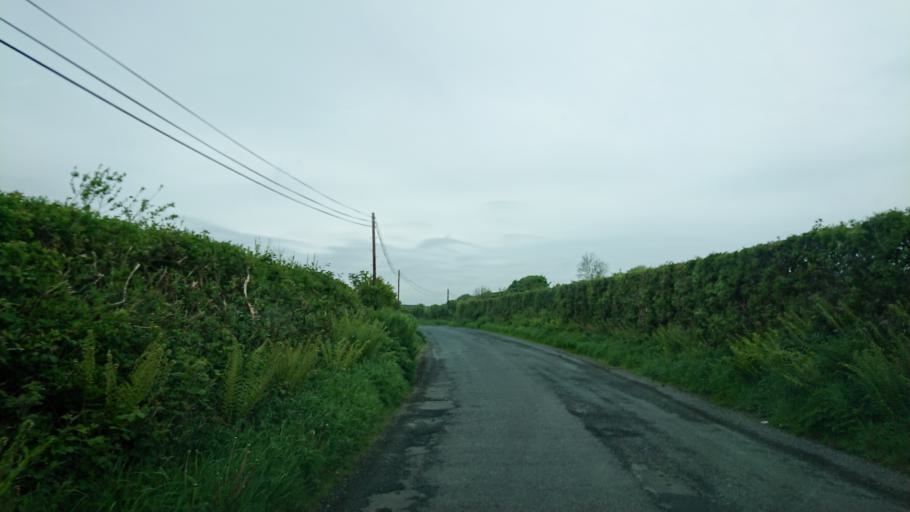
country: IE
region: Munster
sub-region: Waterford
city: Dunmore East
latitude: 52.2208
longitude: -7.0348
